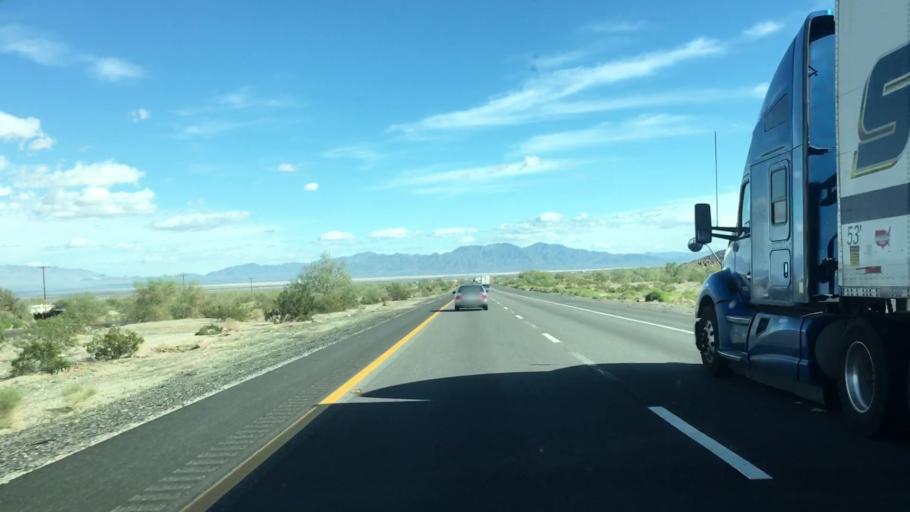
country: US
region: California
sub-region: Imperial County
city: Niland
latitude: 33.7077
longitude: -115.4266
